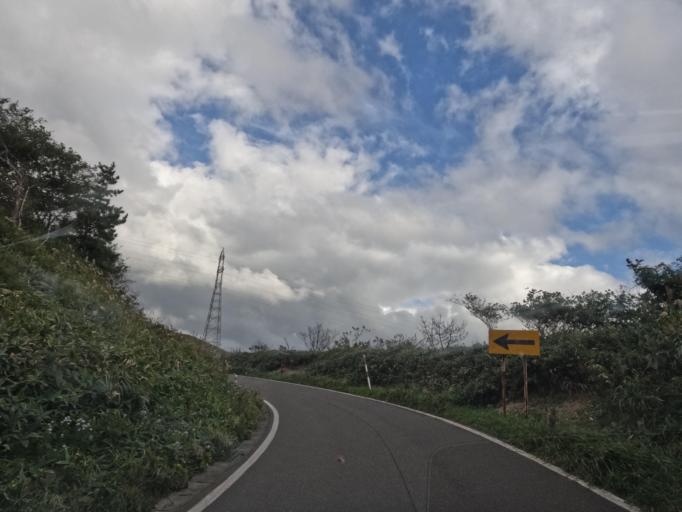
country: JP
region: Hokkaido
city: Muroran
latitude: 42.3187
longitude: 141.0041
